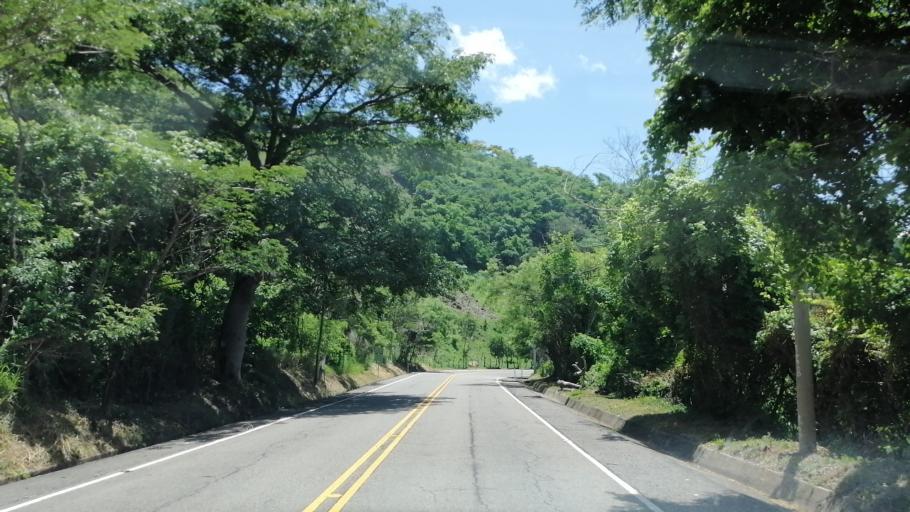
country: SV
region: Chalatenango
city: Nueva Concepcion
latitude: 14.1739
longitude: -89.3120
